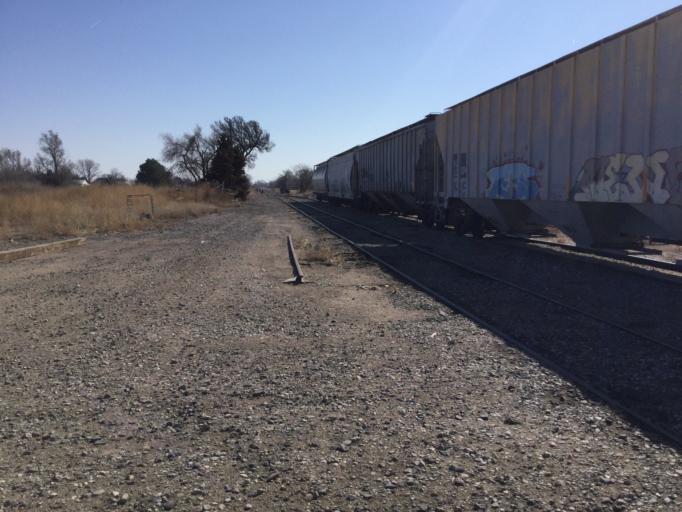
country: US
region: Kansas
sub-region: Rush County
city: La Crosse
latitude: 38.4670
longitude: -99.3175
